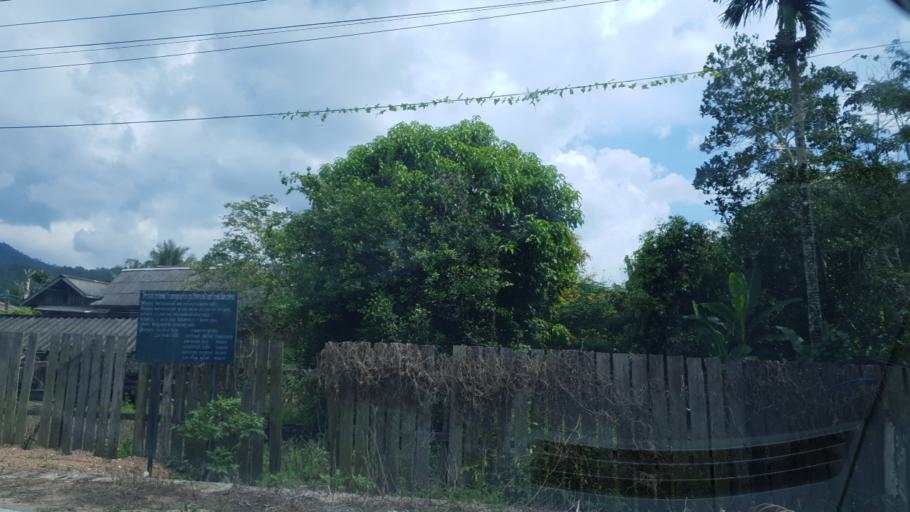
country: TH
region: Mae Hong Son
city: Khun Yuam
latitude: 18.7394
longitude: 97.9264
